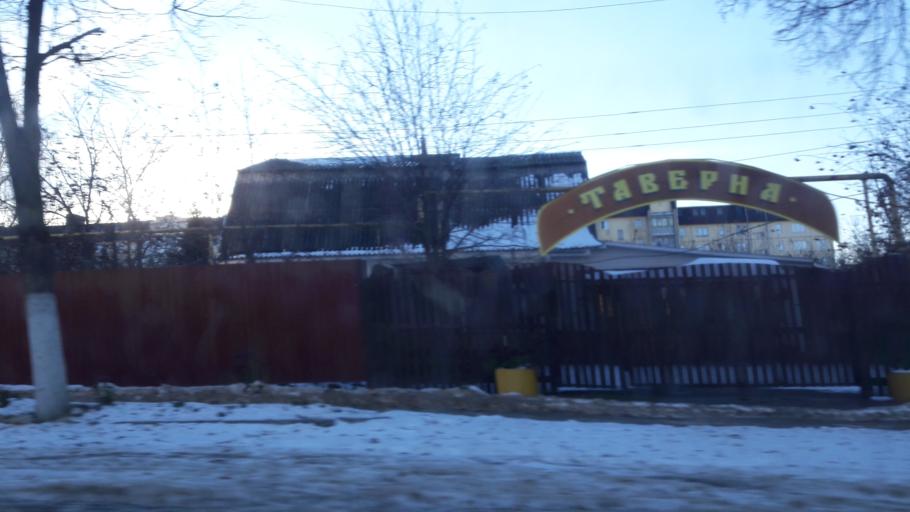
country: RU
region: Tula
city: Gorelki
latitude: 54.2365
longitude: 37.6219
